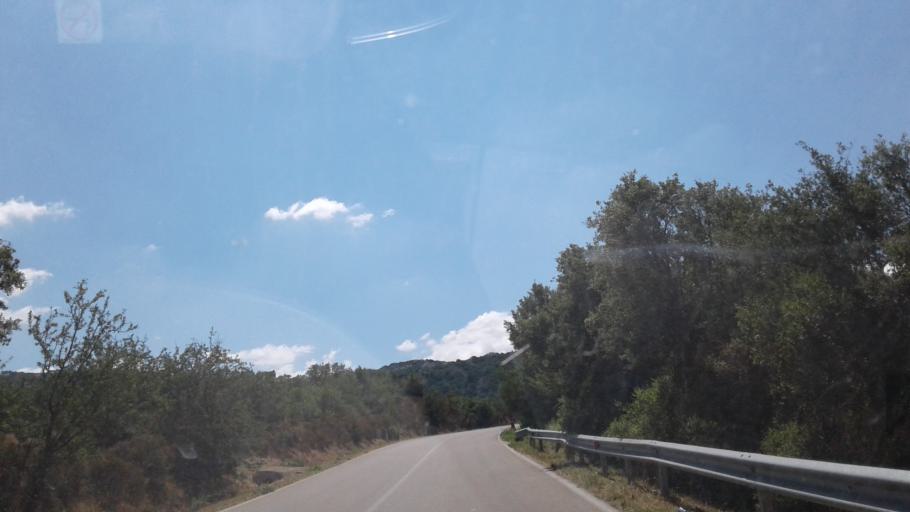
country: IT
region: Sardinia
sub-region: Provincia di Olbia-Tempio
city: Luras
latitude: 40.9565
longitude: 9.2062
